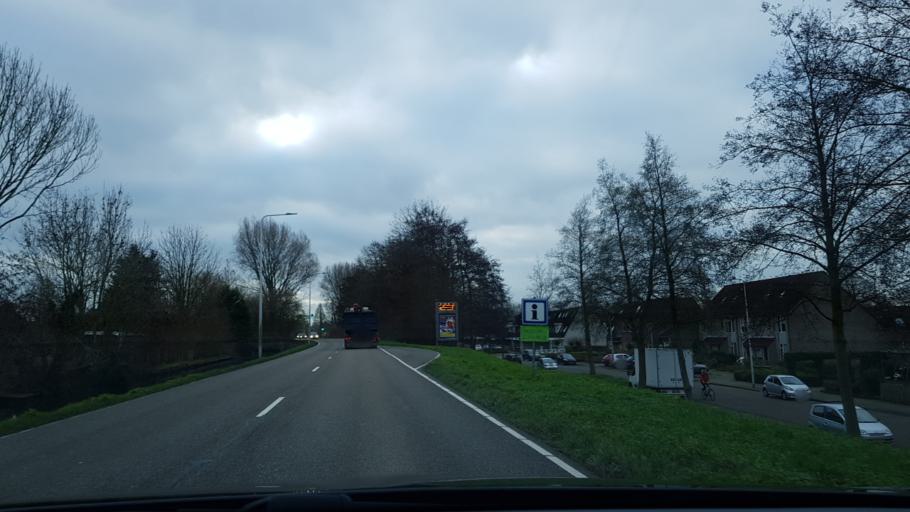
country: NL
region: South Holland
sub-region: Gemeente Kaag en Braassem
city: Oude Wetering
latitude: 52.2143
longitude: 4.6441
